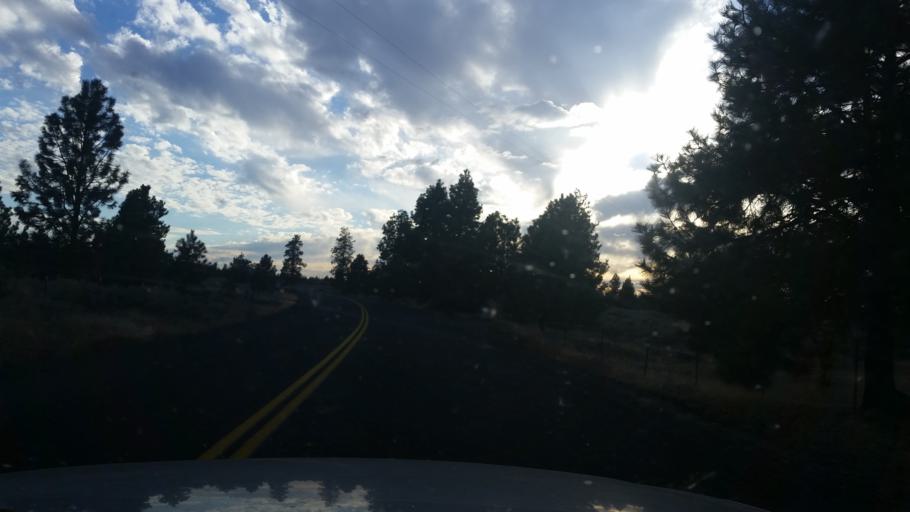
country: US
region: Washington
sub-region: Spokane County
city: Medical Lake
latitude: 47.4528
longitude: -117.8145
